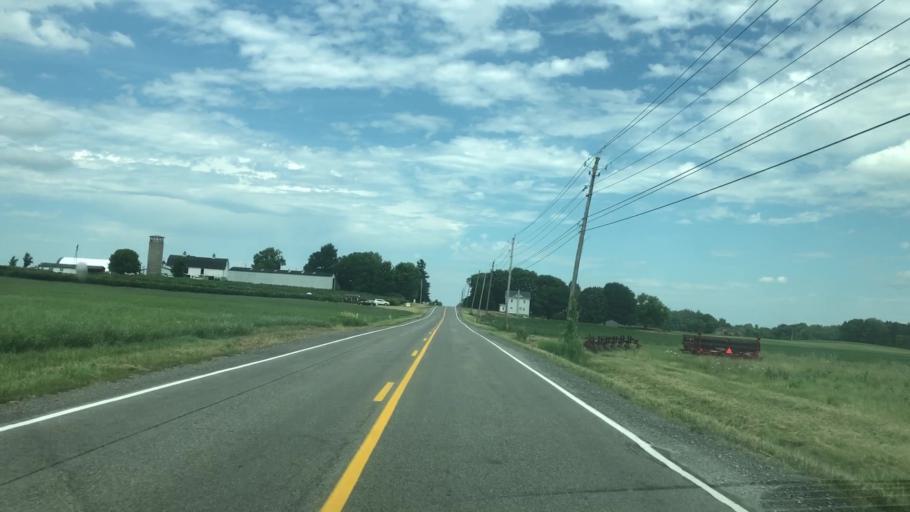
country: US
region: New York
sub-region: Monroe County
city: Webster
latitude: 43.1685
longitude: -77.4005
